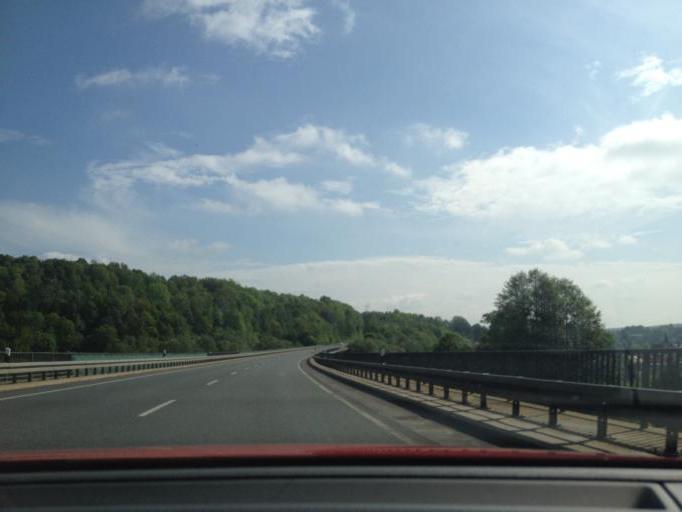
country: DE
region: Bavaria
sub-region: Upper Franconia
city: Arzberg
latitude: 50.0576
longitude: 12.1733
